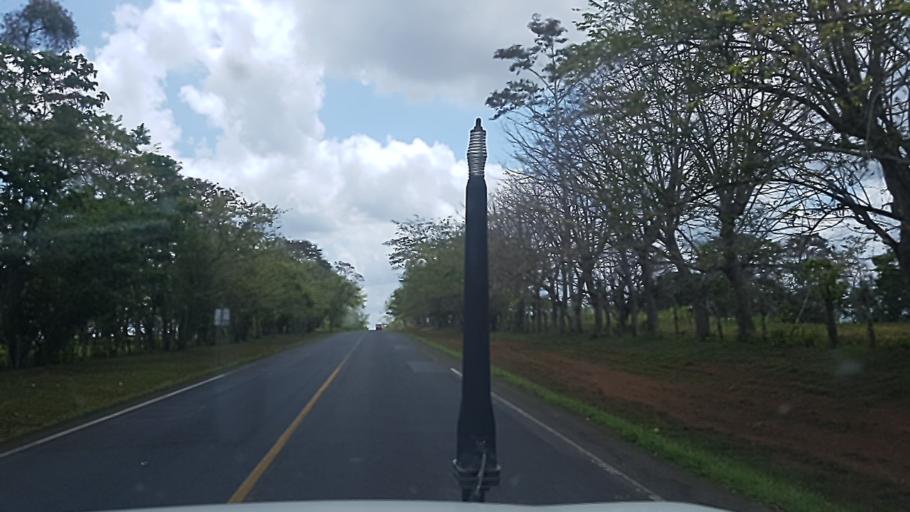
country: NI
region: Atlantico Sur
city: Muelle de los Bueyes
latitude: 11.8945
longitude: -84.6475
